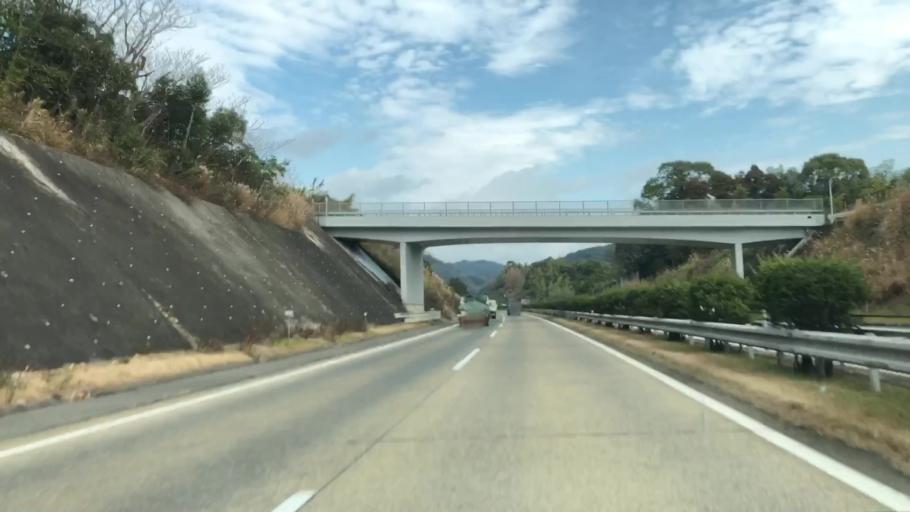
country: JP
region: Saga Prefecture
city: Kanzakimachi-kanzaki
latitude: 33.3315
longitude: 130.3197
